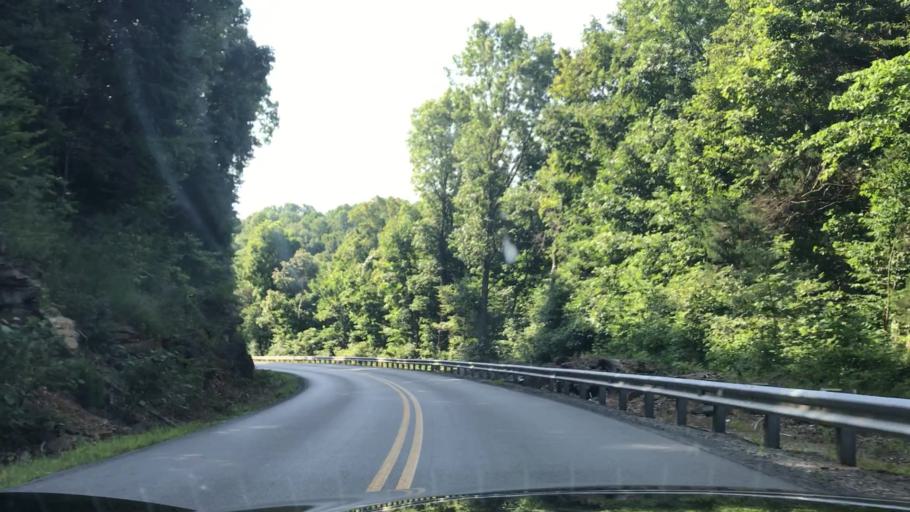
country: US
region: Kentucky
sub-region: Green County
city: Greensburg
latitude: 37.2267
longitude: -85.6817
